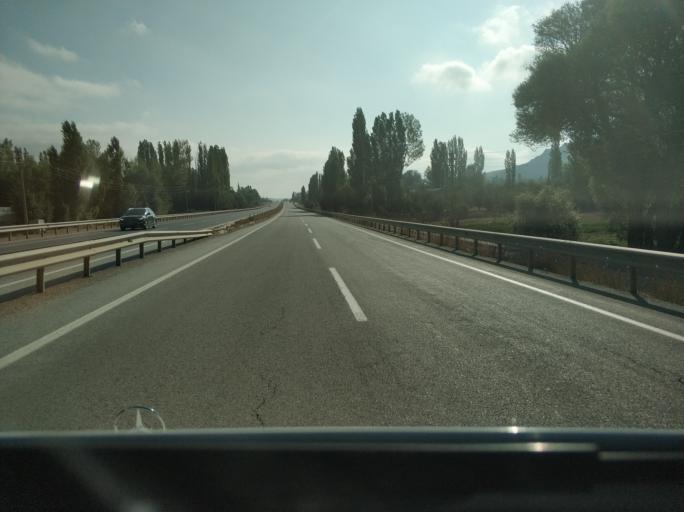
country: TR
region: Sivas
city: Yildizeli
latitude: 39.8402
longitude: 36.4627
